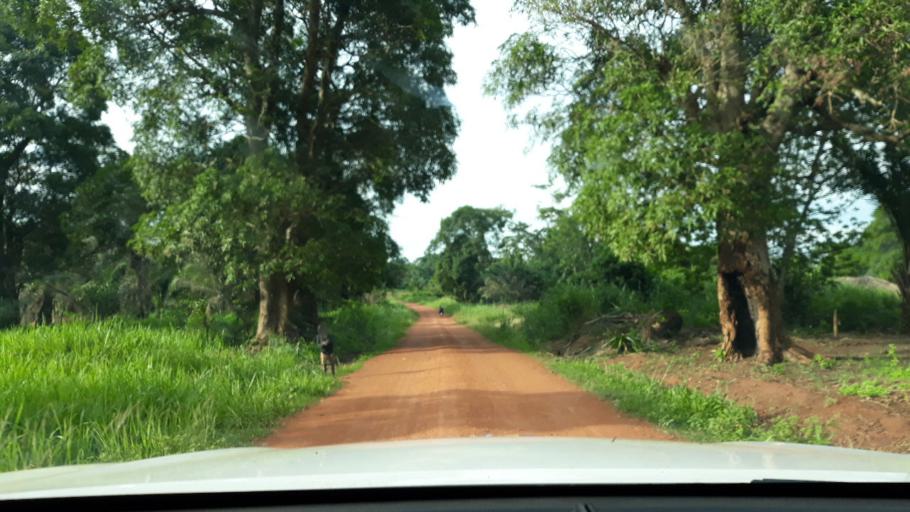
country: CD
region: Equateur
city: Libenge
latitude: 3.9240
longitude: 18.6962
